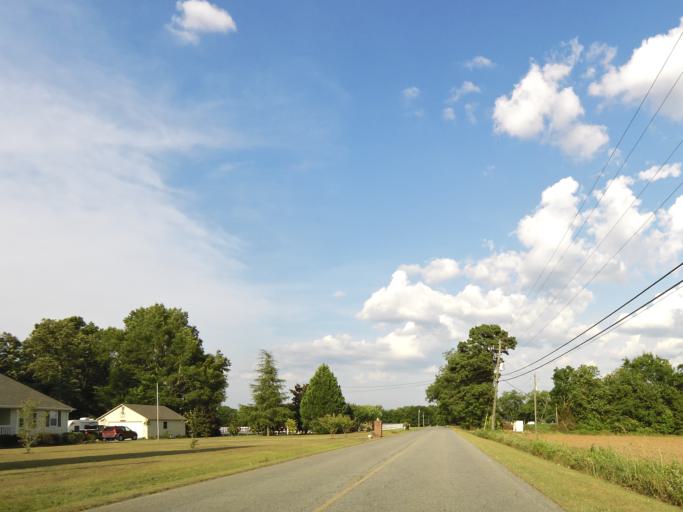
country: US
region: Georgia
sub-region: Houston County
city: Centerville
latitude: 32.7167
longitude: -83.6860
